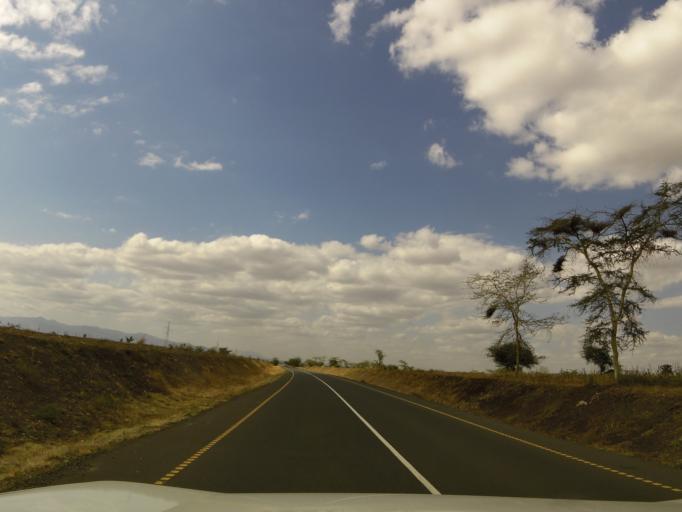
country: TZ
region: Arusha
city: Mto wa Mbu
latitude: -3.6045
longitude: 36.0496
